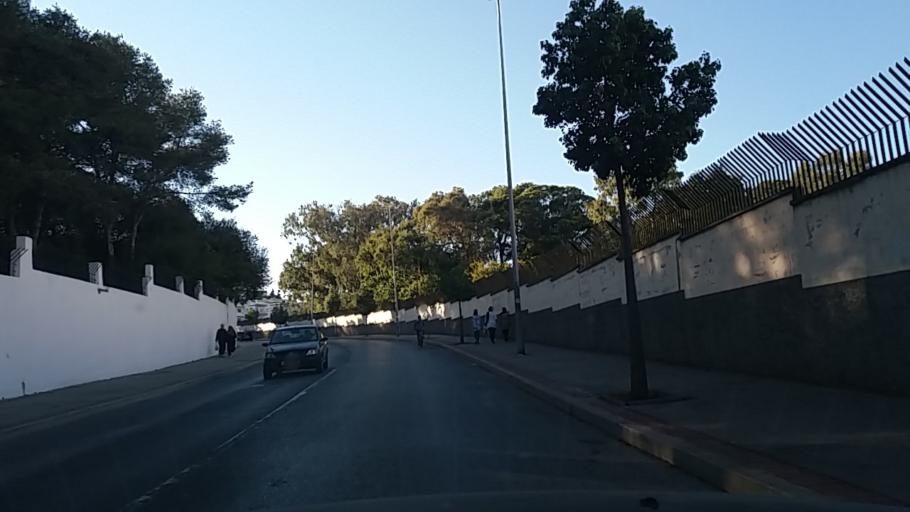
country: MA
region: Tanger-Tetouan
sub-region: Tanger-Assilah
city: Tangier
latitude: 35.7756
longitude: -5.8226
